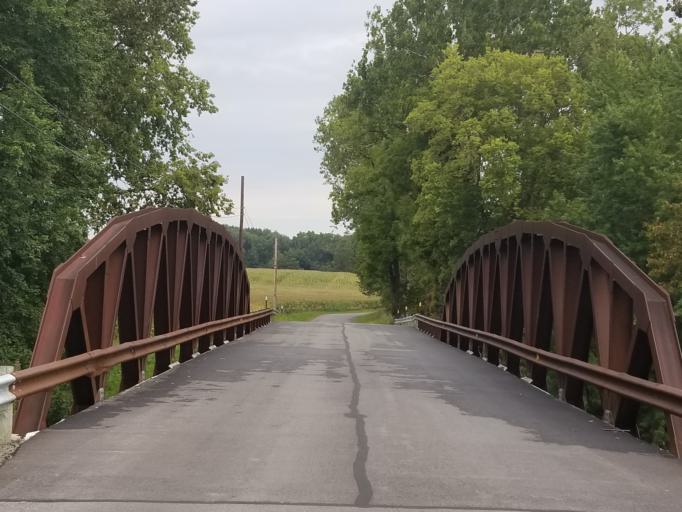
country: US
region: Ohio
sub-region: Wyandot County
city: Upper Sandusky
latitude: 40.7600
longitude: -83.1883
